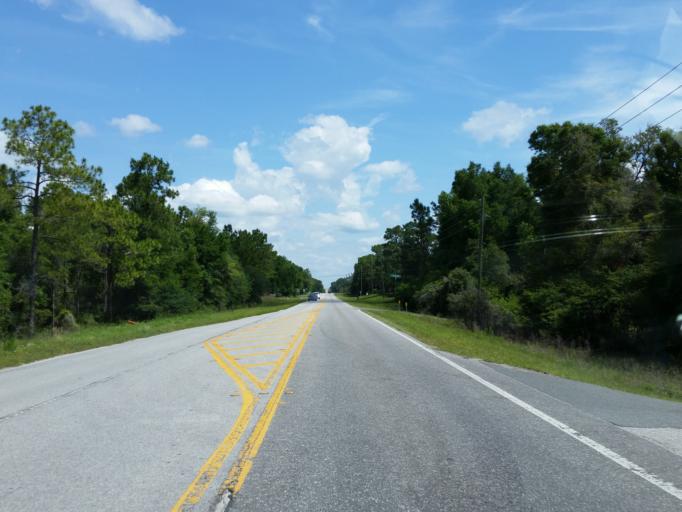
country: US
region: Florida
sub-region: Citrus County
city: Inverness Highlands South
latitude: 28.7974
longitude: -82.3530
